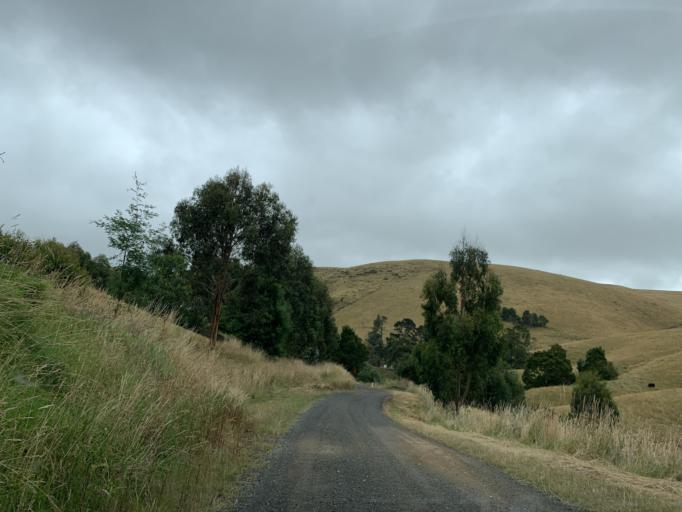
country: AU
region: Victoria
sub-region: Baw Baw
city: Warragul
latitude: -38.3289
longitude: 145.8470
